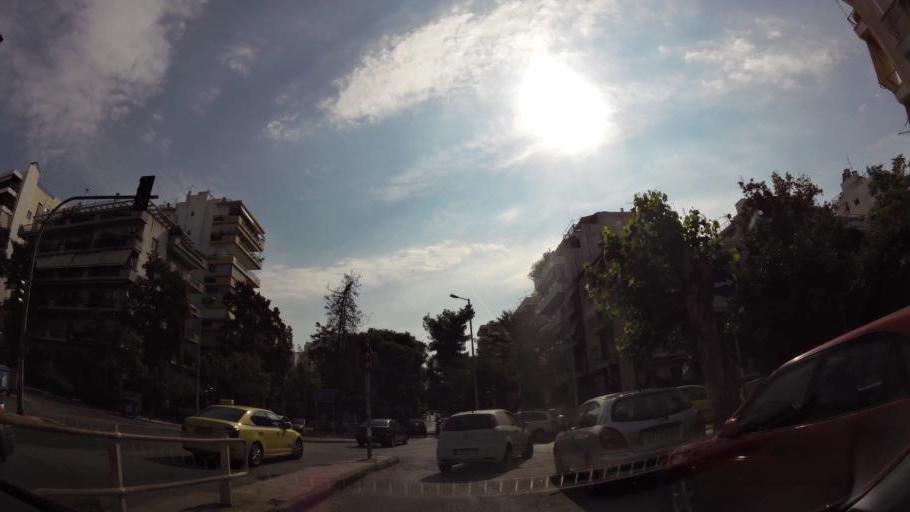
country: GR
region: Attica
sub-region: Nomarchia Athinas
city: Nea Smyrni
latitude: 37.9532
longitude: 23.7137
